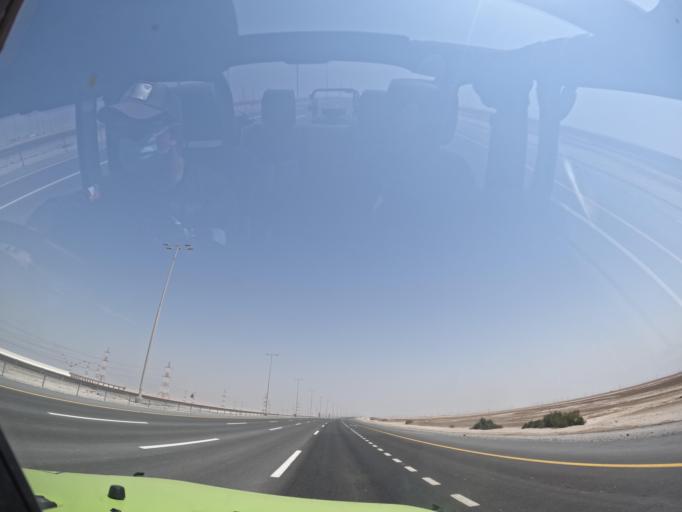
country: AE
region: Abu Dhabi
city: Abu Dhabi
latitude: 24.1537
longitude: 54.2553
